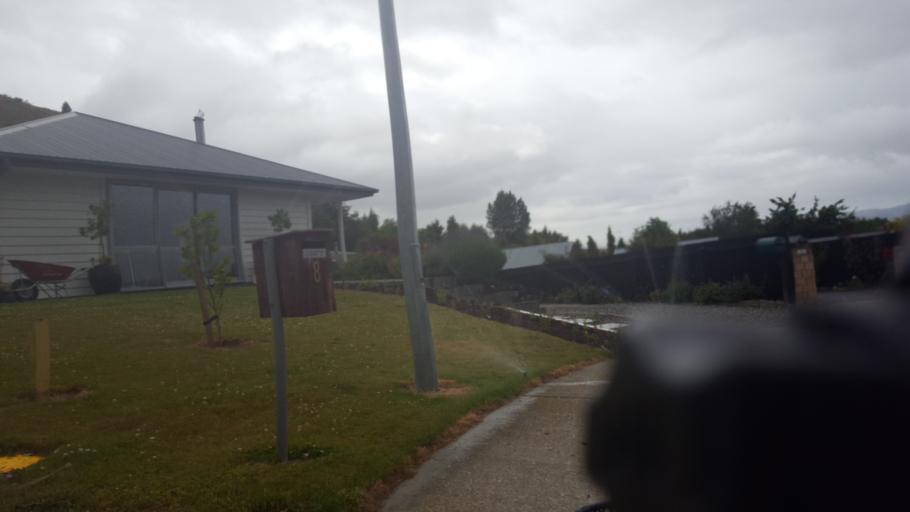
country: NZ
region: Otago
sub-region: Queenstown-Lakes District
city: Wanaka
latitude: -45.1893
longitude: 169.3290
